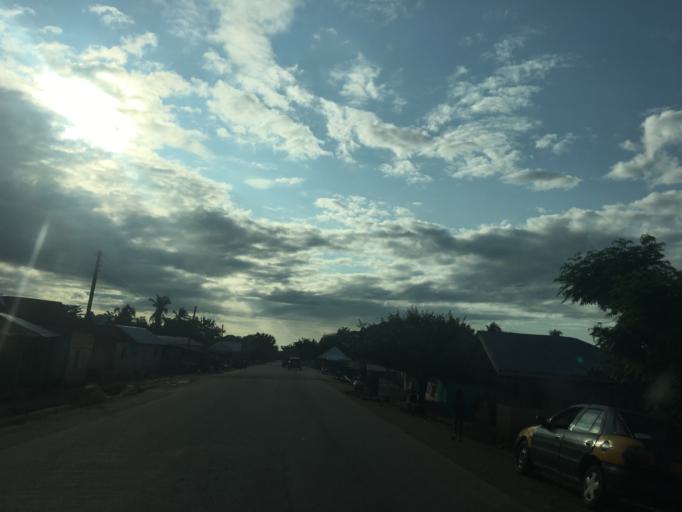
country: GH
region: Western
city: Bibiani
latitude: 6.2915
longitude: -2.2326
